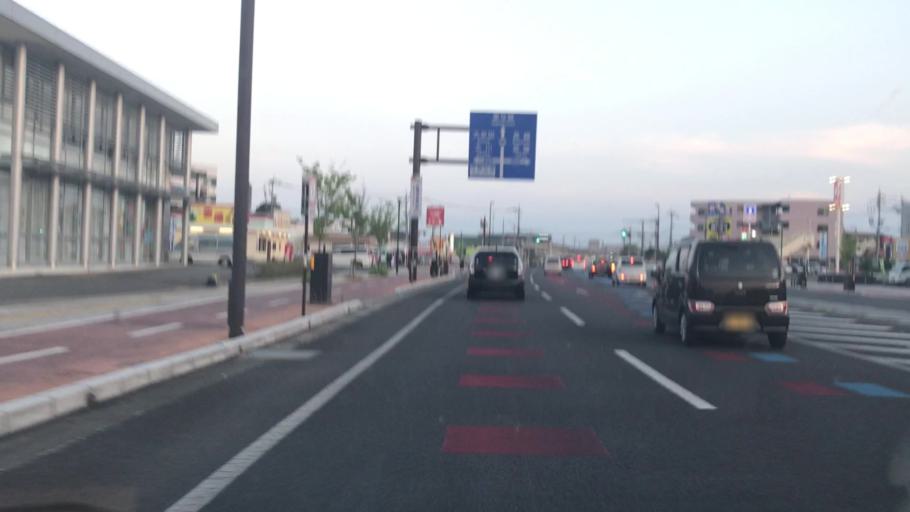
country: JP
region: Saga Prefecture
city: Saga-shi
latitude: 33.2408
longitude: 130.2944
